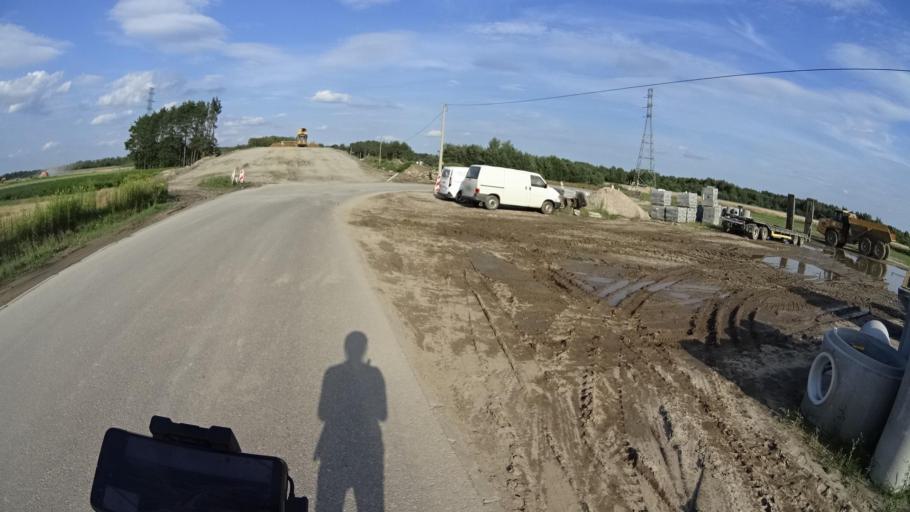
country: PL
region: Masovian Voivodeship
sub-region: Powiat piaseczynski
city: Tarczyn
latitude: 51.9942
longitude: 20.8793
